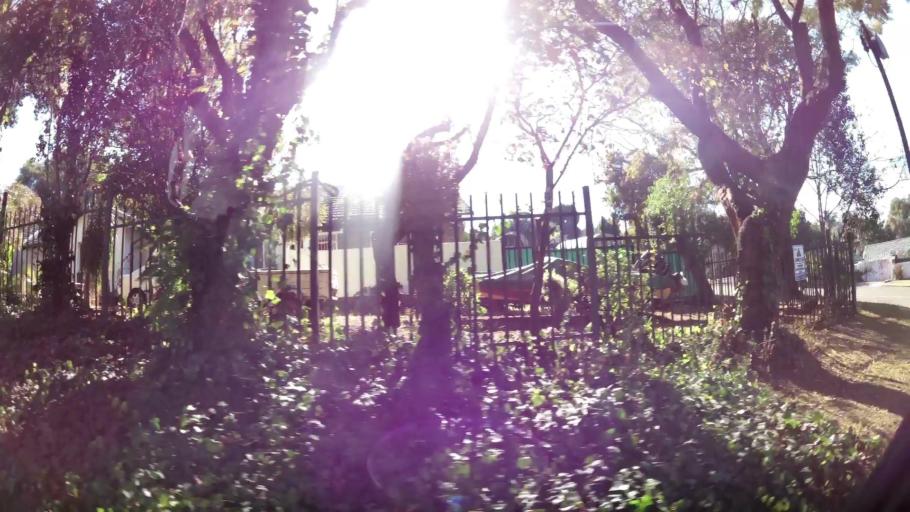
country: ZA
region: Gauteng
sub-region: City of Johannesburg Metropolitan Municipality
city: Roodepoort
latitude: -26.1197
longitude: 27.8633
